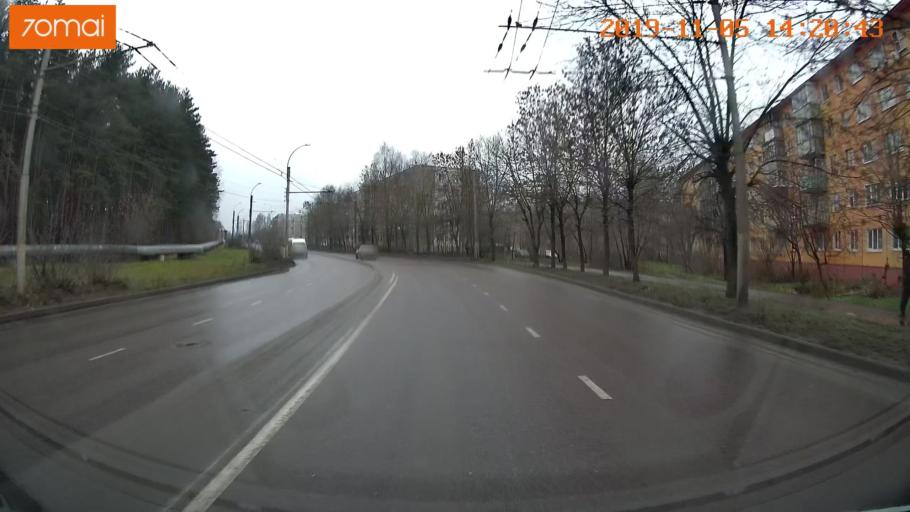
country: RU
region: Ivanovo
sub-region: Gorod Ivanovo
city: Ivanovo
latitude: 56.9576
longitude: 41.0175
